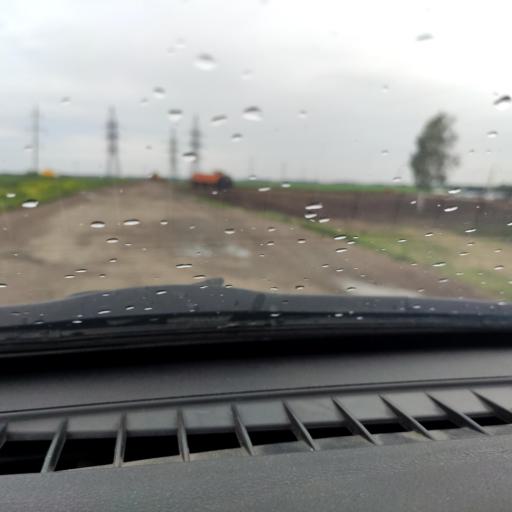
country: RU
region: Samara
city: Tol'yatti
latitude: 53.5933
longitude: 49.4385
